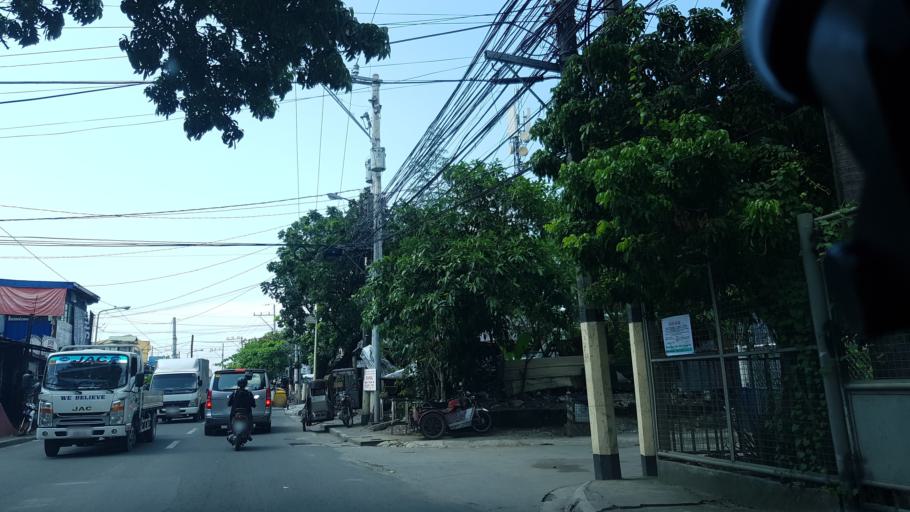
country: PH
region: Calabarzon
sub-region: Province of Rizal
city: Las Pinas
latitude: 14.4694
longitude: 120.9795
